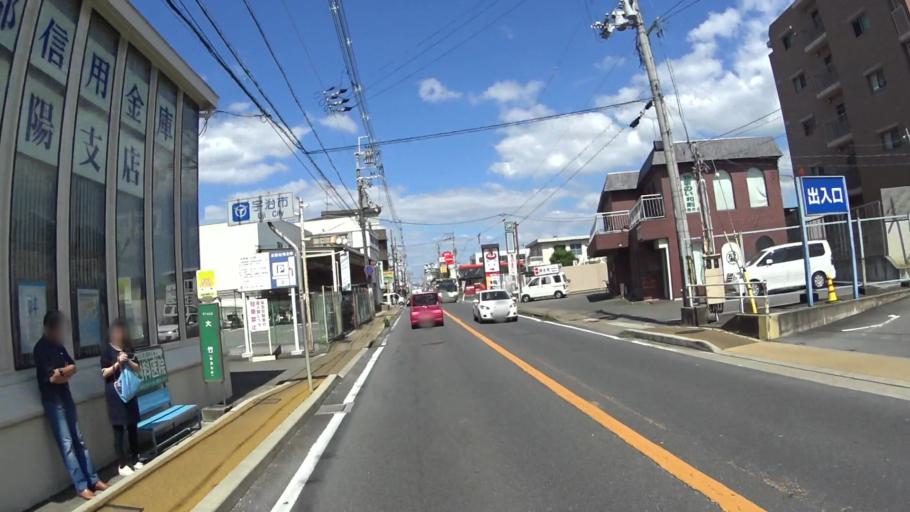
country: JP
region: Kyoto
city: Uji
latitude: 34.8683
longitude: 135.7774
